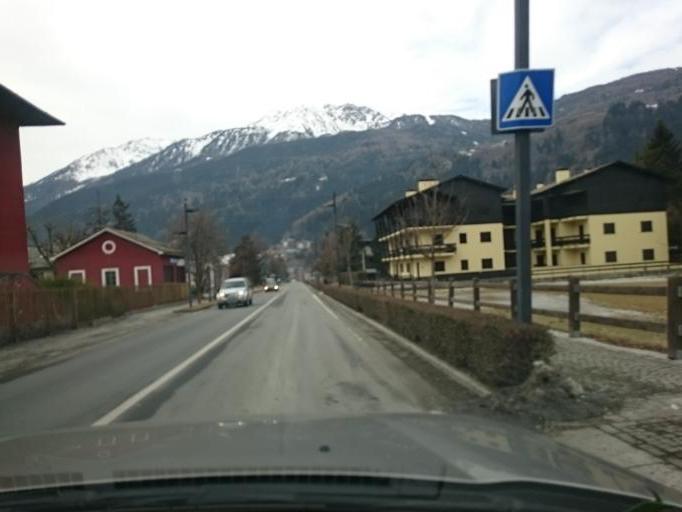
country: IT
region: Lombardy
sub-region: Provincia di Sondrio
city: Bormio
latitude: 46.4631
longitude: 10.3641
